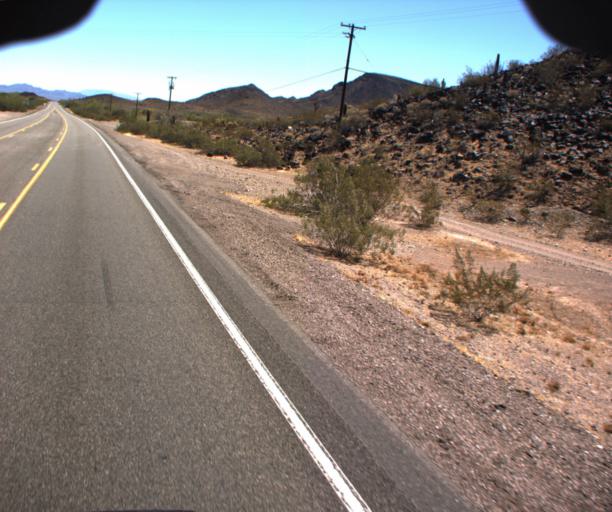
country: US
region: Arizona
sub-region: La Paz County
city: Quartzsite
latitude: 33.6793
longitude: -113.9459
